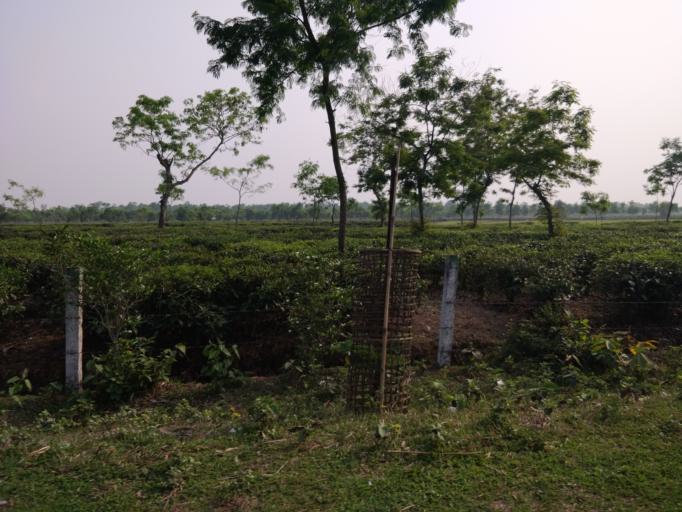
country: IN
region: Tripura
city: Khowai
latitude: 24.1292
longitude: 91.3790
